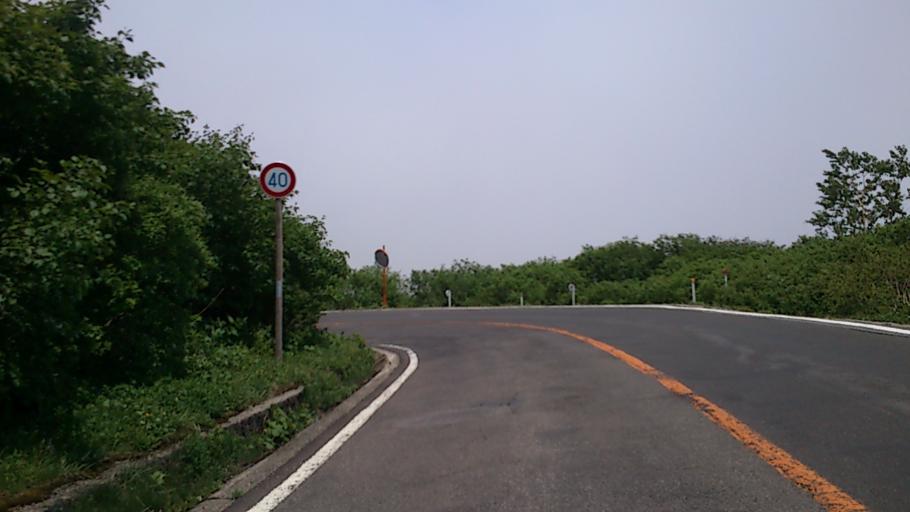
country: JP
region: Yamagata
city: Yamagata-shi
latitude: 38.1278
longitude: 140.4599
